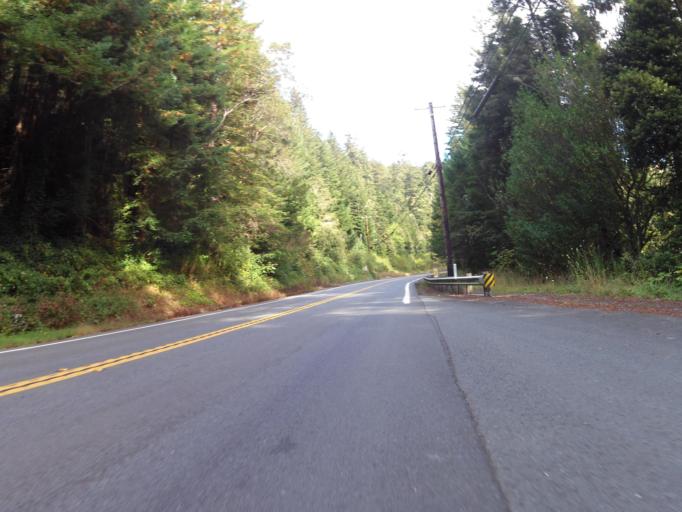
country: US
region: California
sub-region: Del Norte County
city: Bertsch-Oceanview
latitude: 41.8145
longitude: -124.0852
